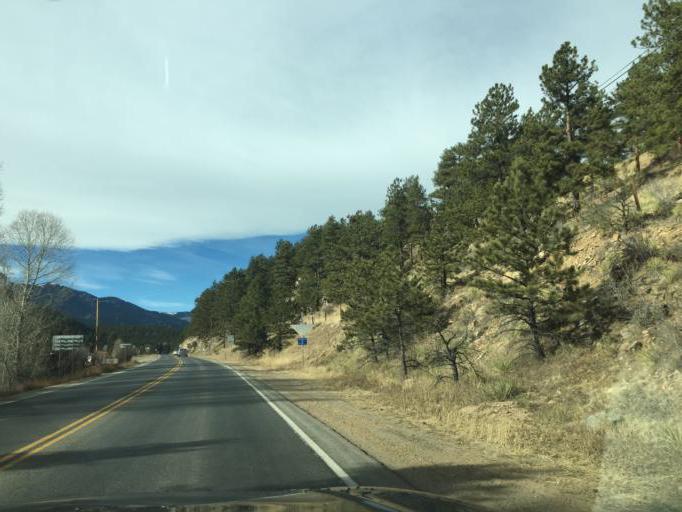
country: US
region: Colorado
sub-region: Jefferson County
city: Evergreen
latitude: 39.4068
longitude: -105.4801
